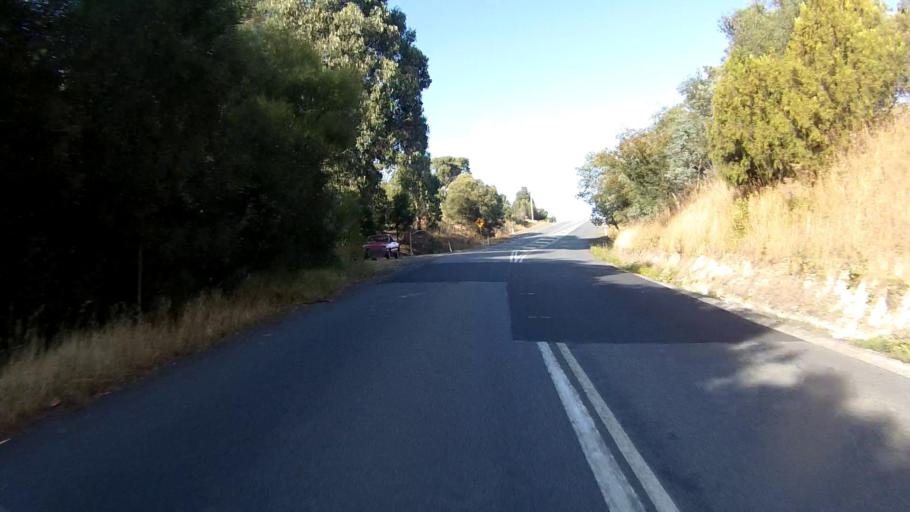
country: AU
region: Tasmania
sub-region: Derwent Valley
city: New Norfolk
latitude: -42.7627
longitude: 147.1333
